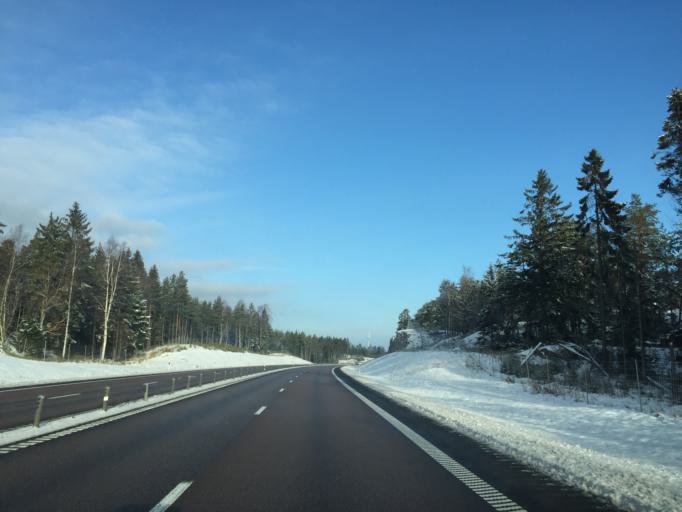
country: SE
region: Vaestra Goetaland
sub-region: Tanums Kommun
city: Tanumshede
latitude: 58.7924
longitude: 11.2785
